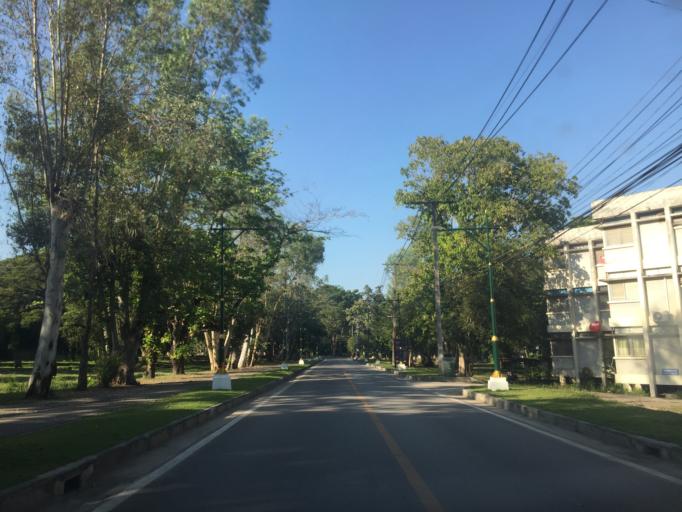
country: TH
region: Chiang Mai
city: Chiang Mai
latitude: 18.7970
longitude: 98.9503
